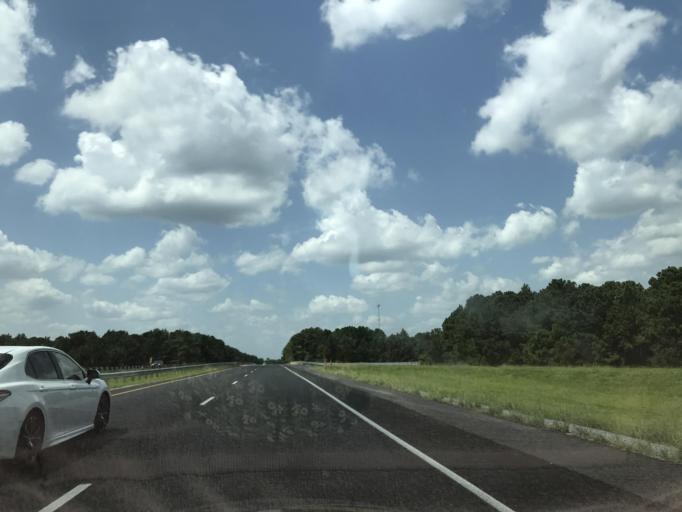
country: US
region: North Carolina
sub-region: Duplin County
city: Warsaw
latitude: 34.9463
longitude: -78.0720
